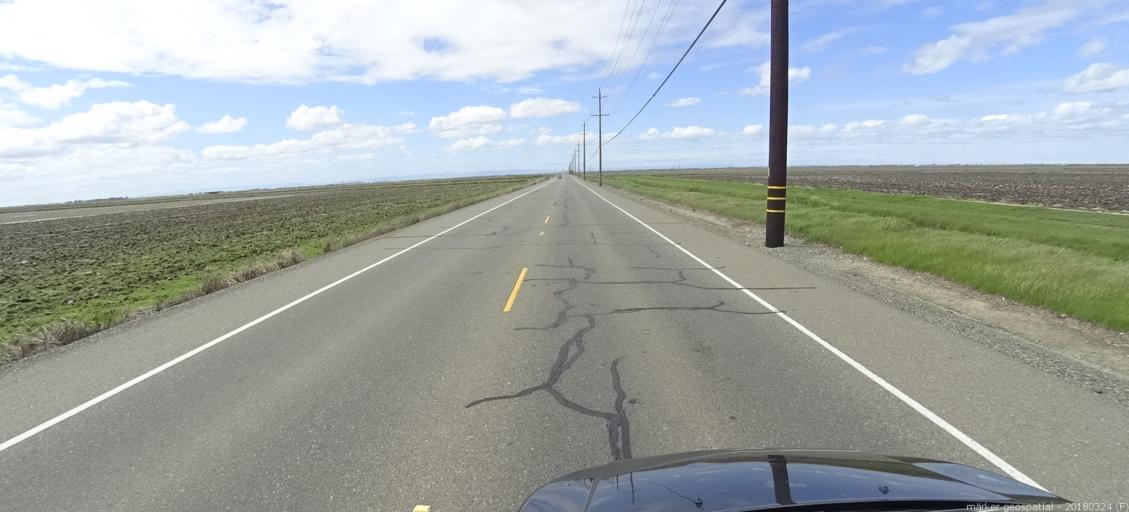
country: US
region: California
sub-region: Sacramento County
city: Elverta
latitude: 38.7143
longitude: -121.5179
